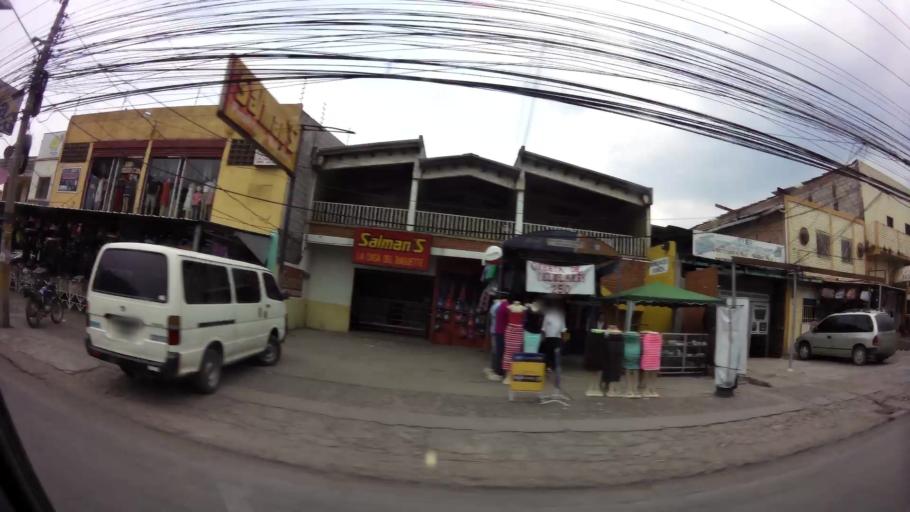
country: HN
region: Francisco Morazan
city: Tegucigalpa
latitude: 14.0988
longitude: -87.2269
